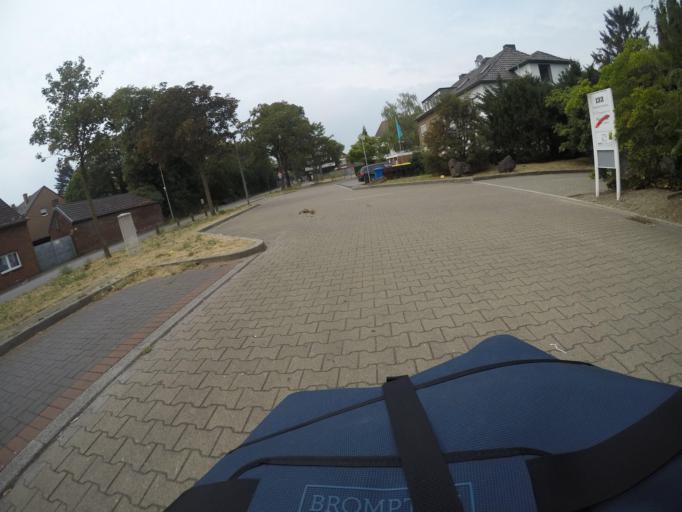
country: DE
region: North Rhine-Westphalia
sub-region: Regierungsbezirk Dusseldorf
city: Dusseldorf
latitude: 51.1757
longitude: 6.7469
